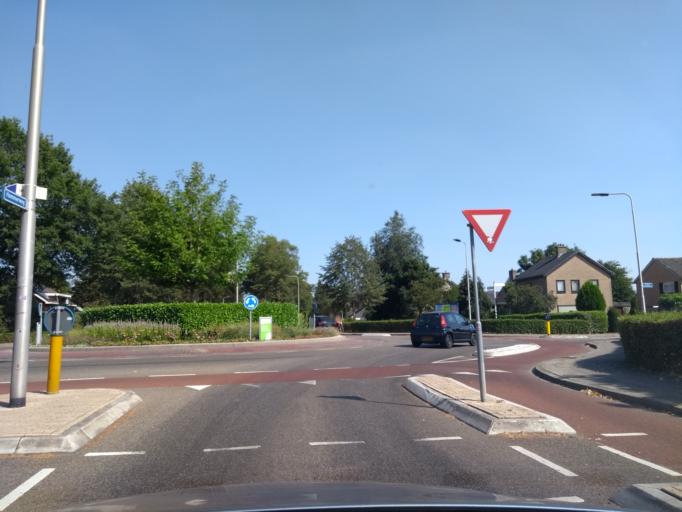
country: NL
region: Overijssel
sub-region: Gemeente Twenterand
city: Vroomshoop
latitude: 52.4618
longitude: 6.5596
